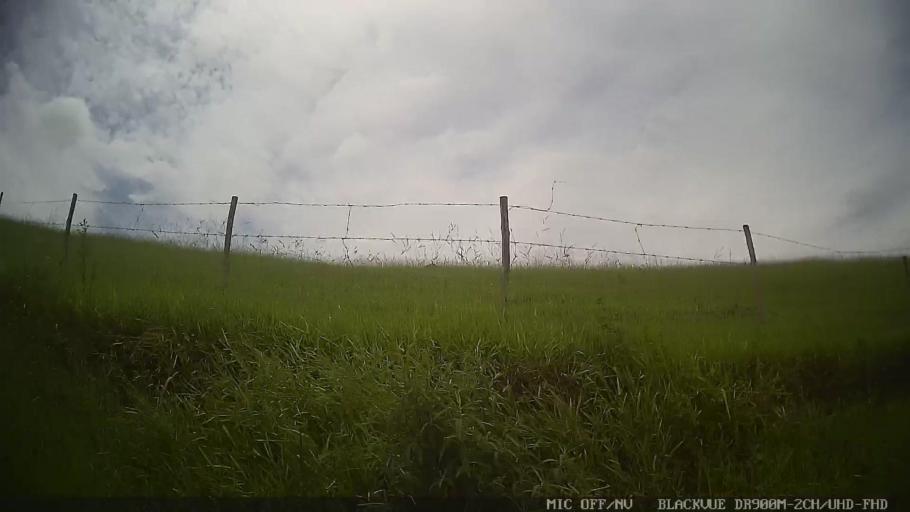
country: BR
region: Sao Paulo
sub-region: Santa Isabel
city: Santa Isabel
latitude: -23.3443
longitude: -46.2273
